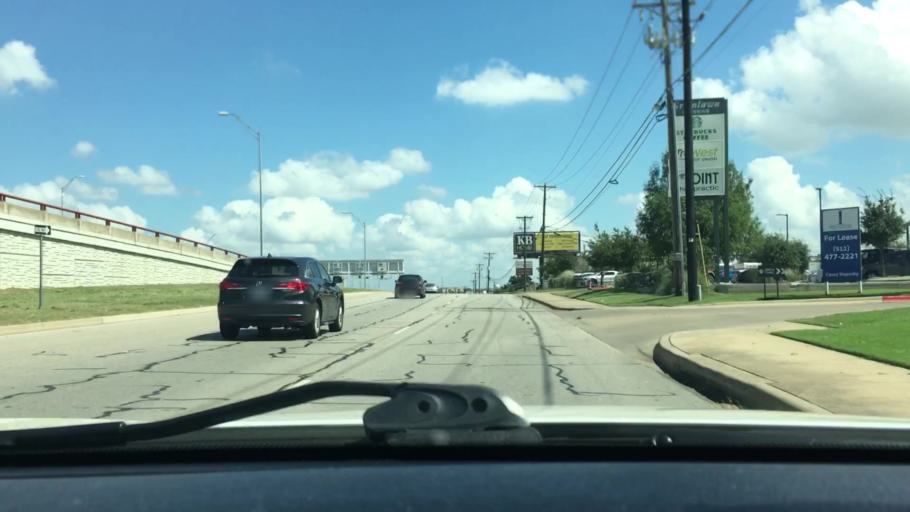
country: US
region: Texas
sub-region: Travis County
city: Windemere
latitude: 30.4830
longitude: -97.6572
